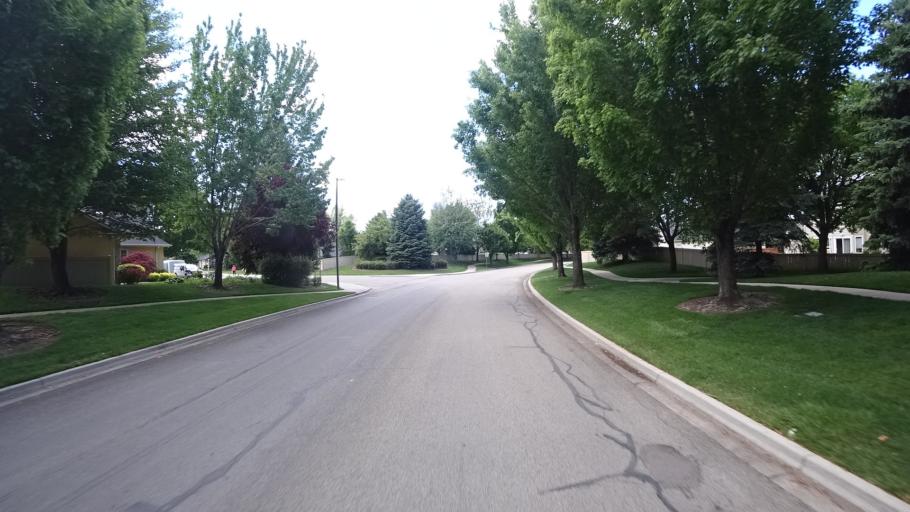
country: US
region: Idaho
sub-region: Ada County
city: Eagle
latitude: 43.6568
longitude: -116.3592
